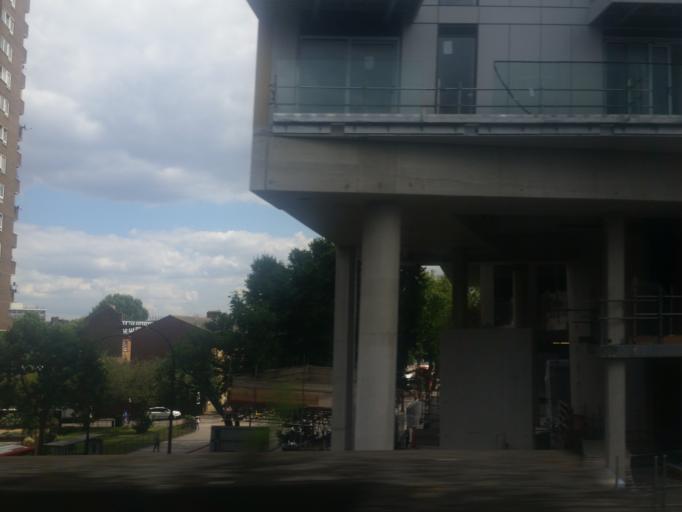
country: GB
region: England
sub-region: Greater London
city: Kennington
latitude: 51.4948
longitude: -0.0983
